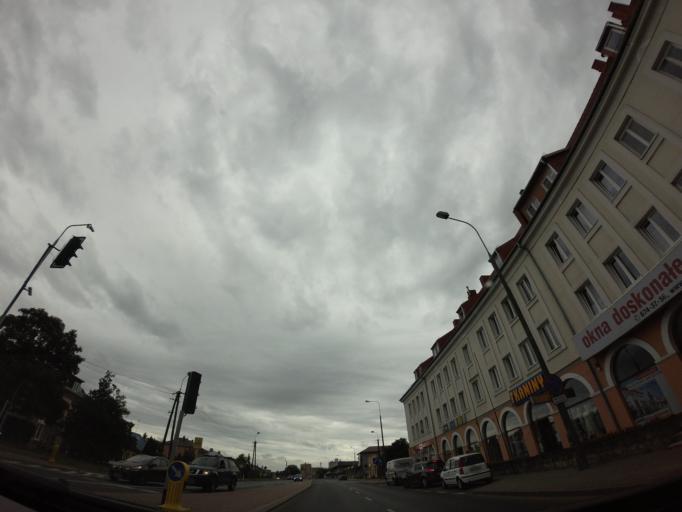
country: PL
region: Masovian Voivodeship
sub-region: Powiat ciechanowski
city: Ciechanow
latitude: 52.8812
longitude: 20.6220
